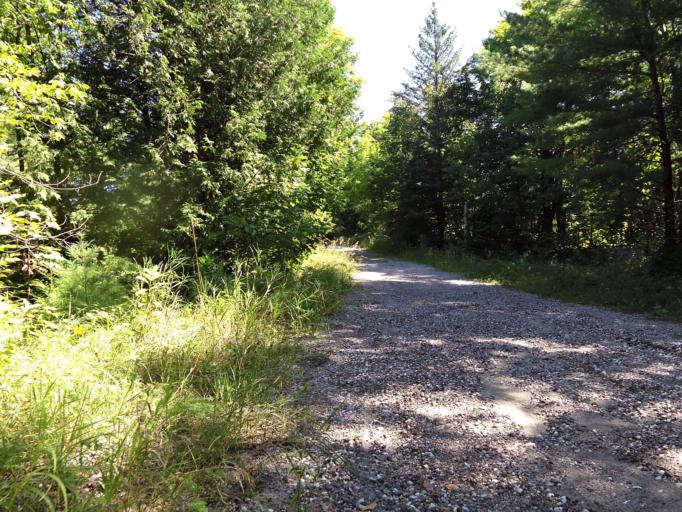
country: CA
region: Ontario
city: Arnprior
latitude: 45.1633
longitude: -76.4867
